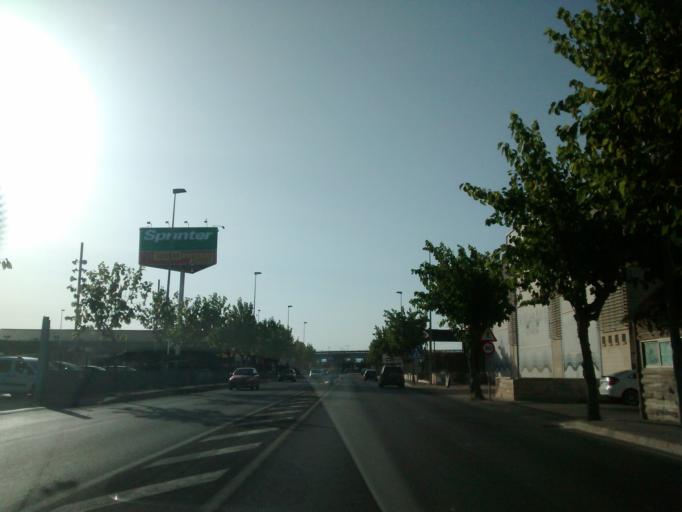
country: ES
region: Valencia
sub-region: Provincia de Alicante
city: Santa Pola
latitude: 38.1988
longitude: -0.5664
